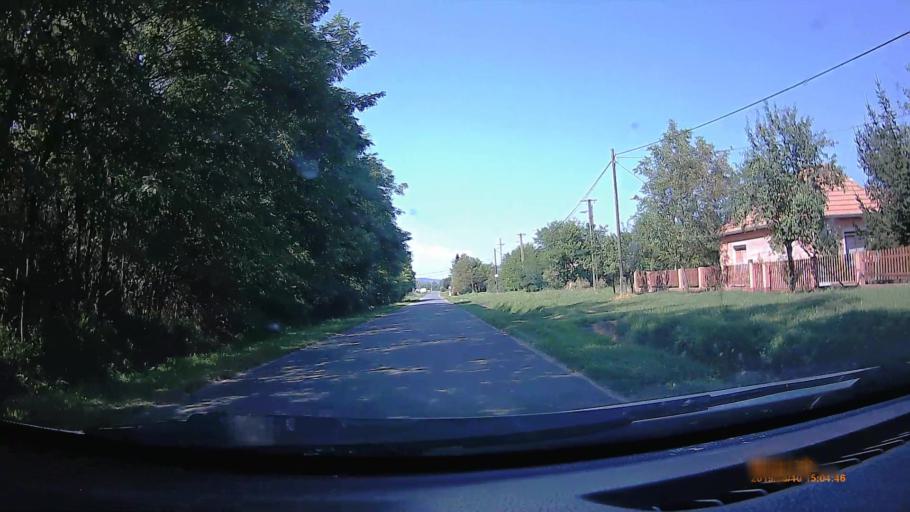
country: HU
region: Somogy
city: Lengyeltoti
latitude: 46.6767
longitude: 17.5660
